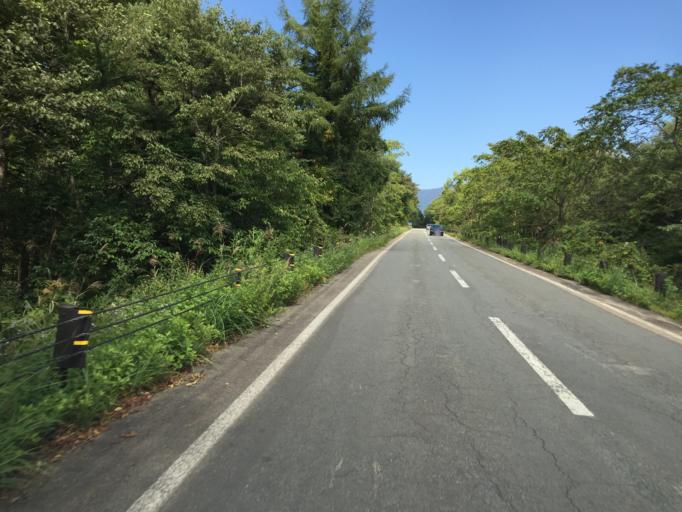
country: JP
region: Fukushima
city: Inawashiro
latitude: 37.6629
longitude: 140.0887
